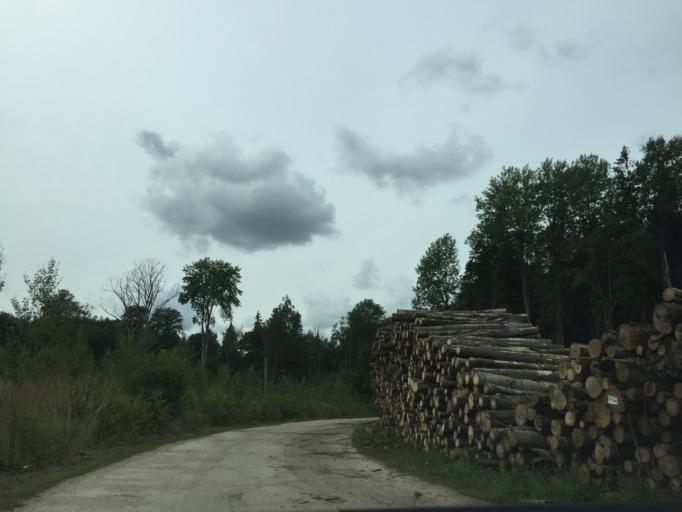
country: LV
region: Lielvarde
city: Lielvarde
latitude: 56.7554
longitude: 24.8615
